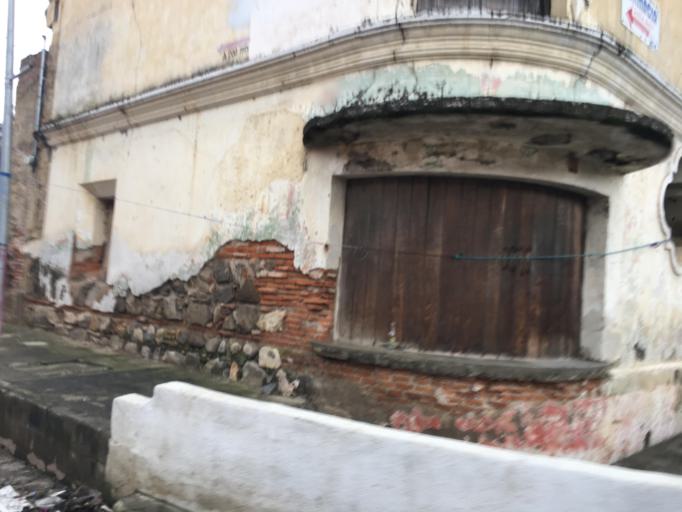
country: GT
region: Sacatepequez
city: Antigua Guatemala
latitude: 14.5725
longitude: -90.7352
